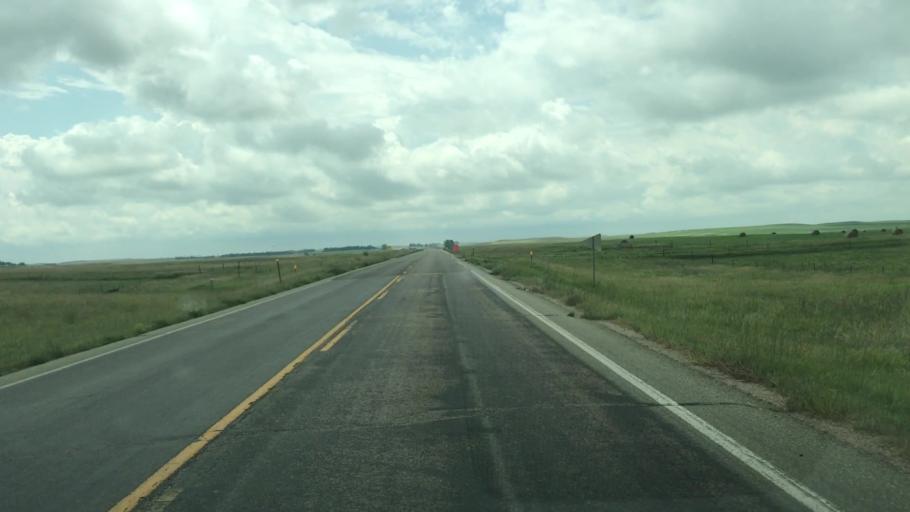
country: US
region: Nebraska
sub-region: Cherry County
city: Valentine
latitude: 43.0614
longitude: -100.5952
